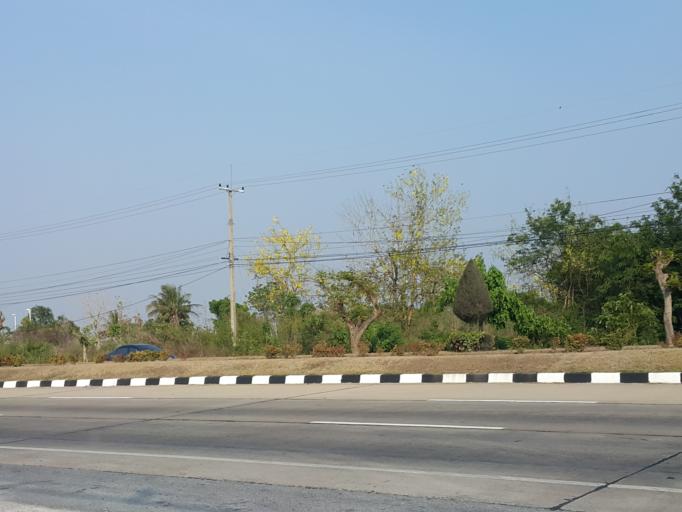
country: TH
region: Suphan Buri
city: Doembang Nangbuat
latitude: 14.8015
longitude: 100.1110
